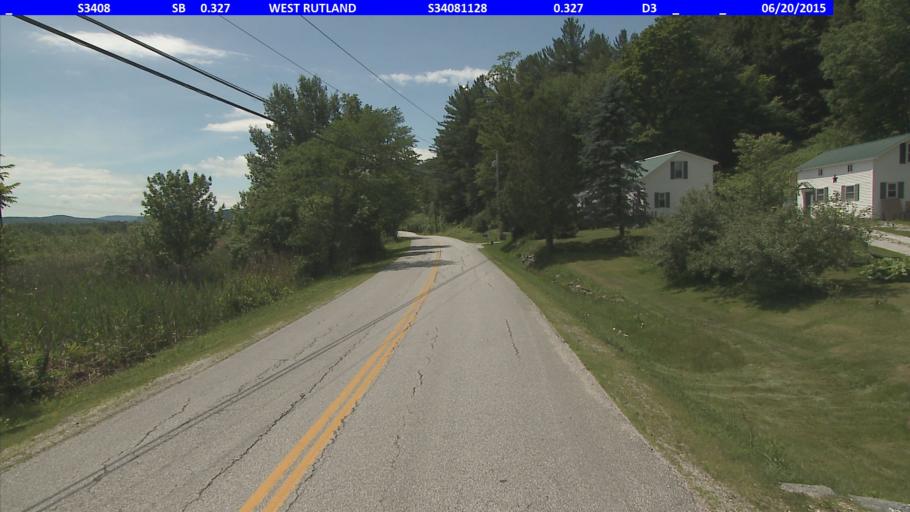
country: US
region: Vermont
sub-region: Rutland County
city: West Rutland
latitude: 43.6149
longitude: -73.0636
